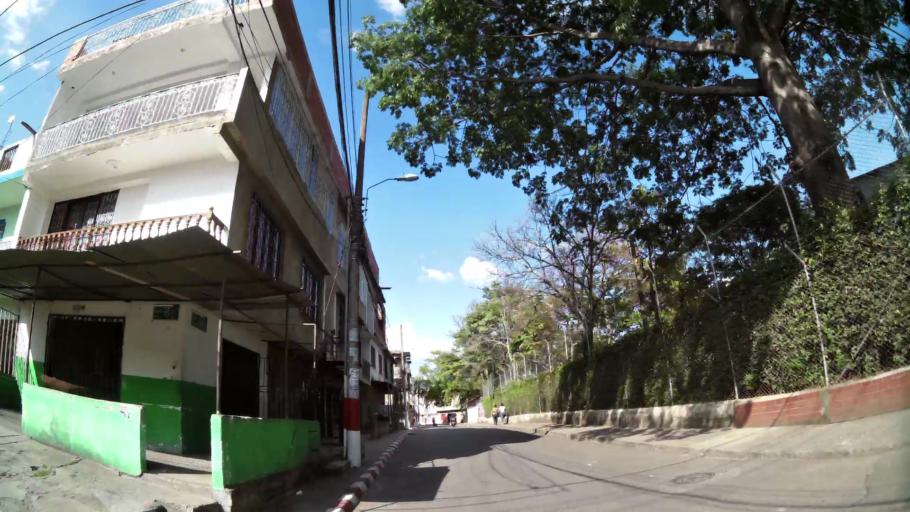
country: CO
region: Valle del Cauca
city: Cali
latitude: 3.4213
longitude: -76.4970
